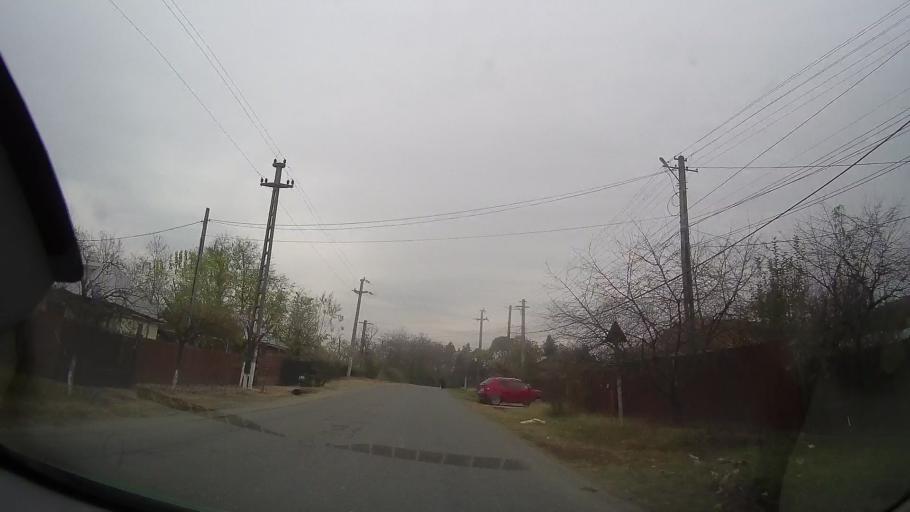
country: RO
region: Prahova
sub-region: Oras Urlati
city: Urlati
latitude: 45.0054
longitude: 26.2276
